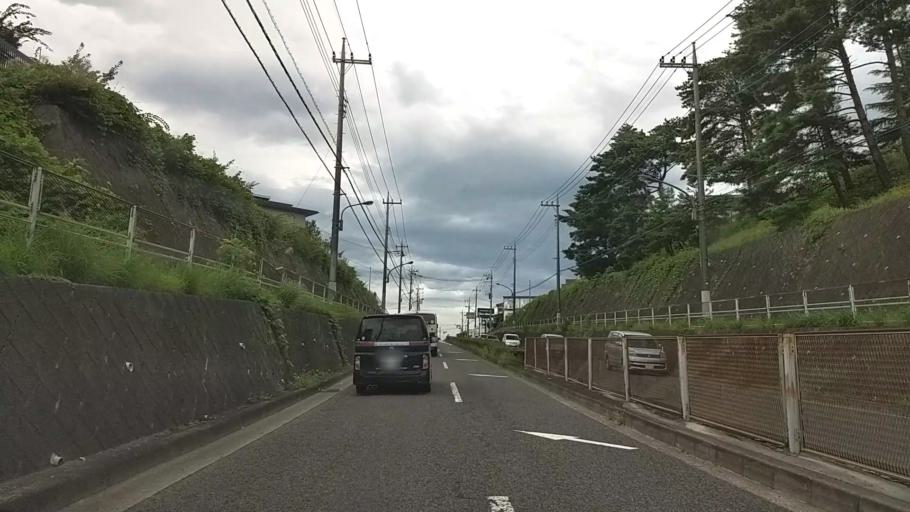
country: JP
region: Tokyo
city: Hachioji
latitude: 35.6346
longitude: 139.3118
